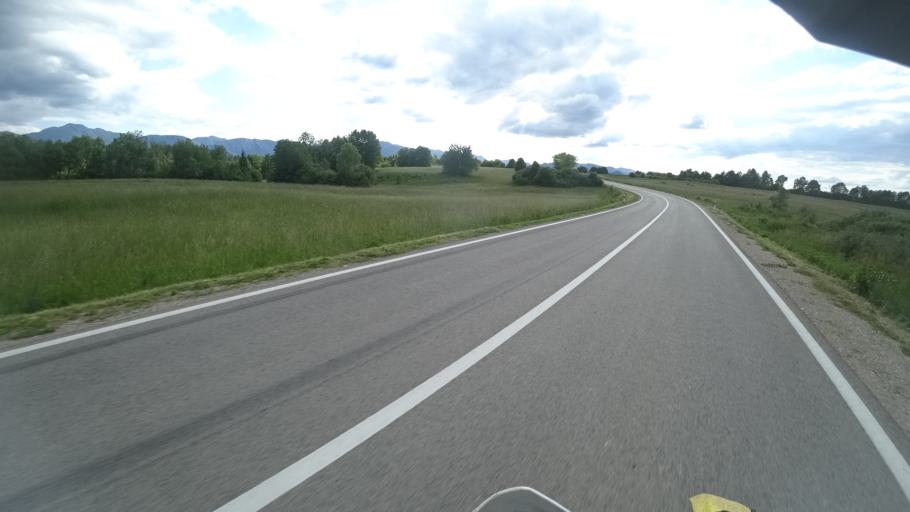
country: HR
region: Licko-Senjska
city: Gospic
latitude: 44.5104
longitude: 15.4326
